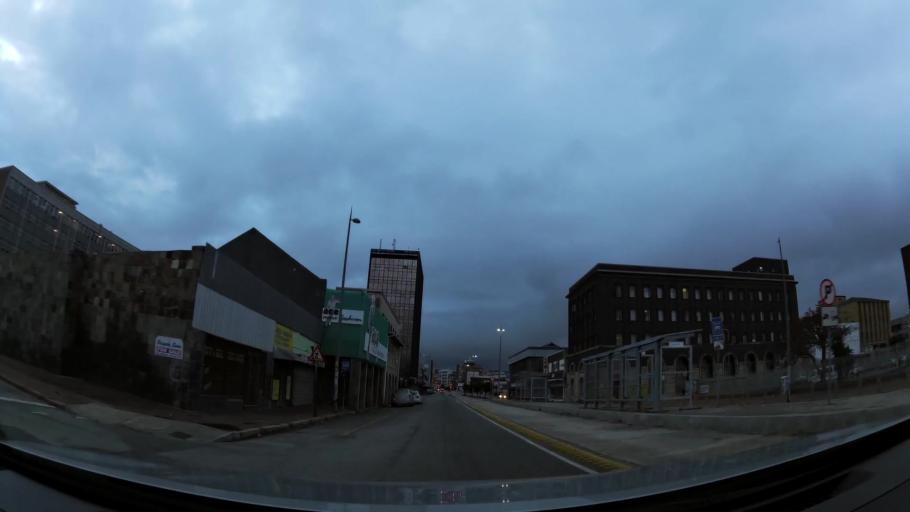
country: ZA
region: Eastern Cape
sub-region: Nelson Mandela Bay Metropolitan Municipality
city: Port Elizabeth
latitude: -33.9441
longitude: 25.6061
